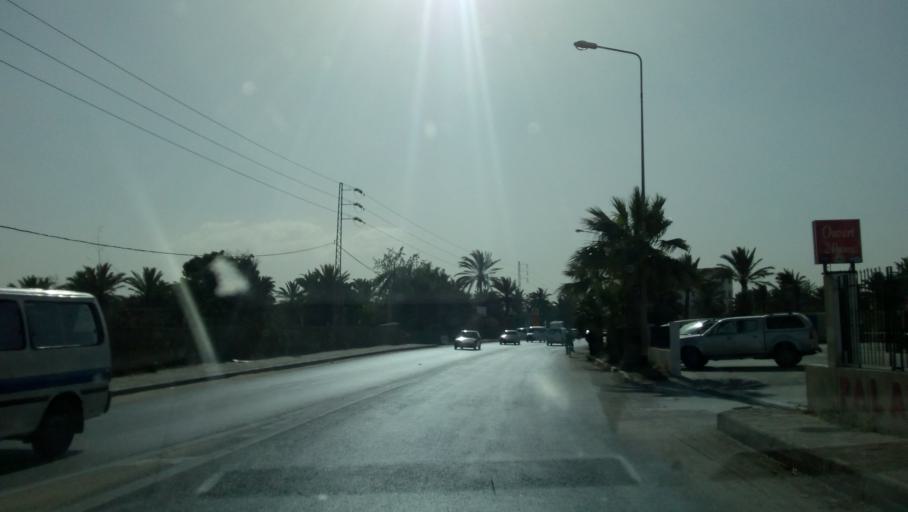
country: TN
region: Qabis
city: Gabes
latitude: 33.8934
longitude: 10.0775
